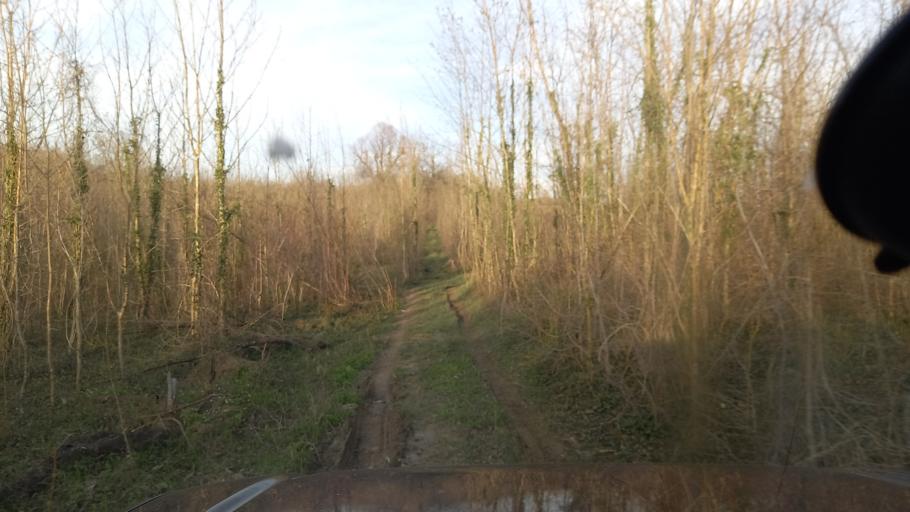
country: RU
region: Krasnodarskiy
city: Arkhipo-Osipovka
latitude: 44.3606
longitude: 38.5609
